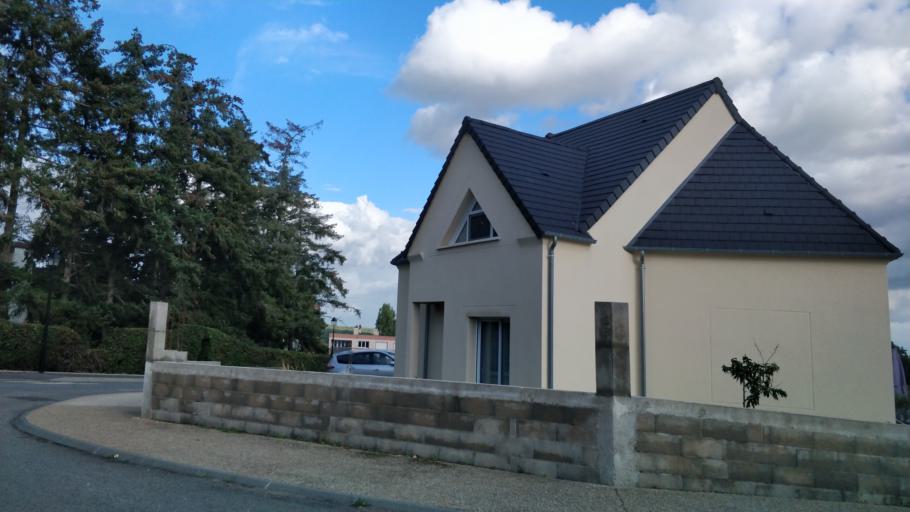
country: FR
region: Ile-de-France
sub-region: Departement de l'Essonne
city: Fontenay-les-Briis
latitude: 48.6221
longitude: 2.1489
